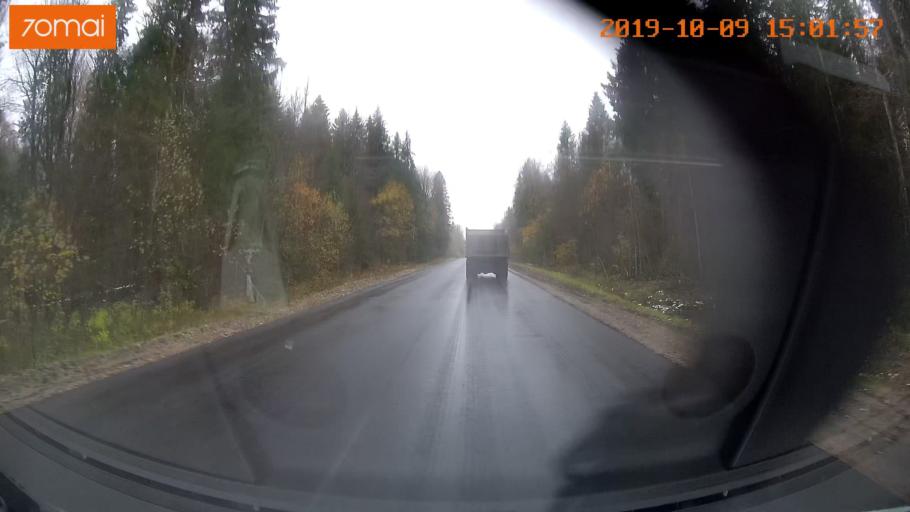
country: RU
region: Kostroma
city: Chistyye Bory
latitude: 58.2912
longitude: 41.6808
